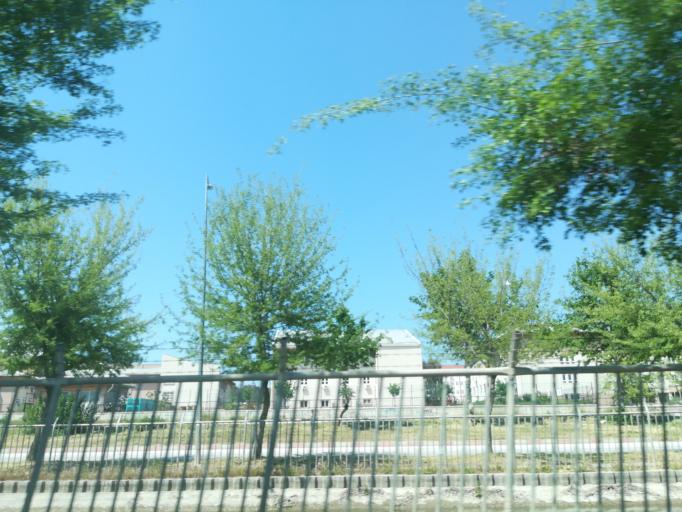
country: TR
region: Adana
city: Adana
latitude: 37.0308
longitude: 35.3492
